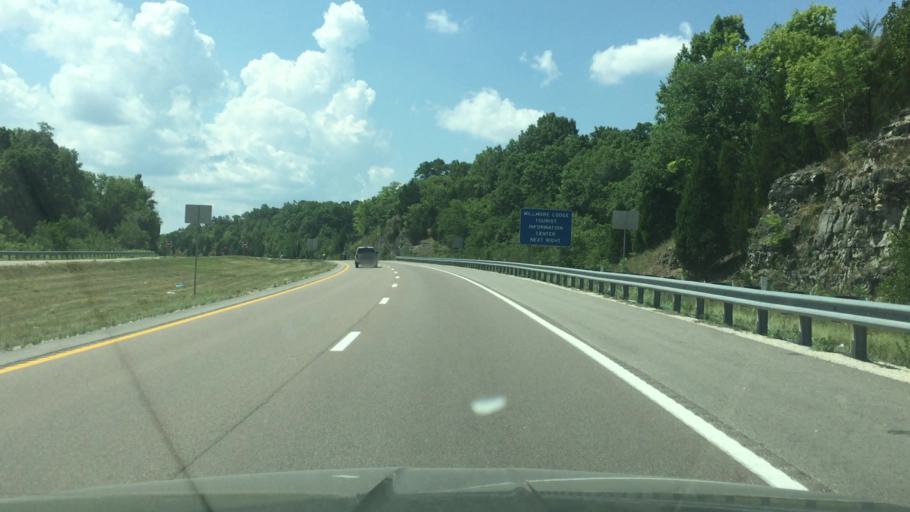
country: US
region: Missouri
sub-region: Miller County
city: Lake Ozark
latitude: 38.2237
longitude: -92.6259
